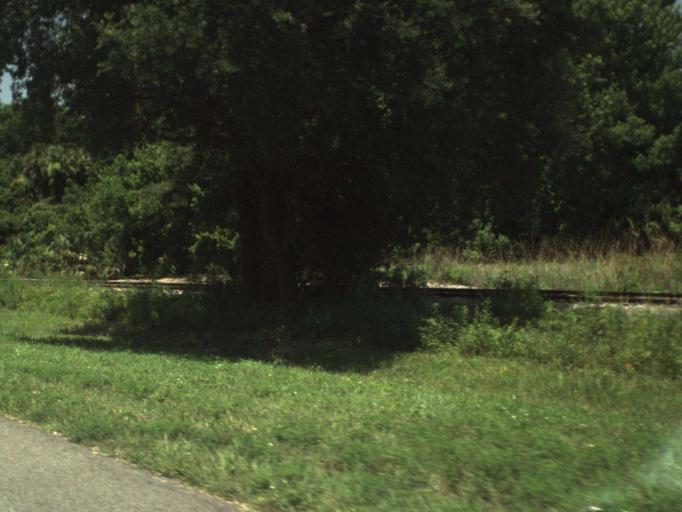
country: US
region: Florida
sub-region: Seminole County
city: Winter Springs
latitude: 28.7126
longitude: -81.3072
